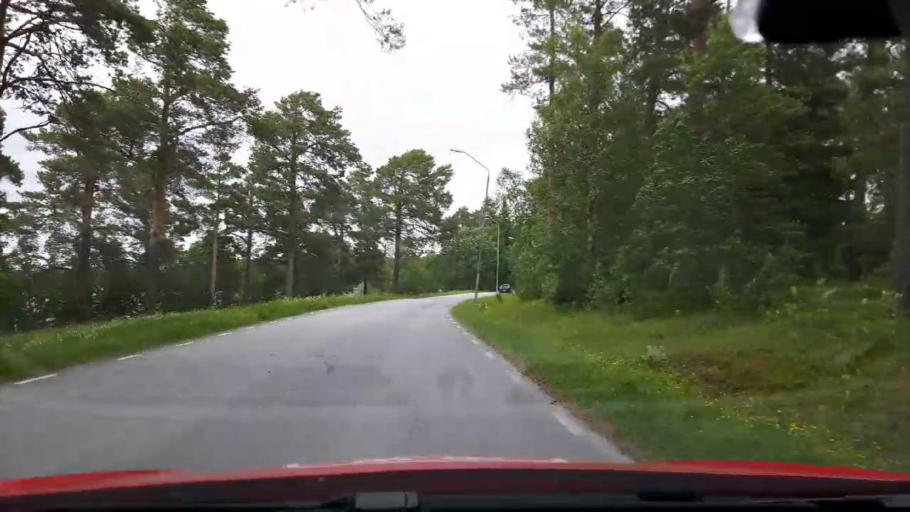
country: SE
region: Jaemtland
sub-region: OEstersunds Kommun
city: Ostersund
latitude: 63.1940
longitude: 14.6329
